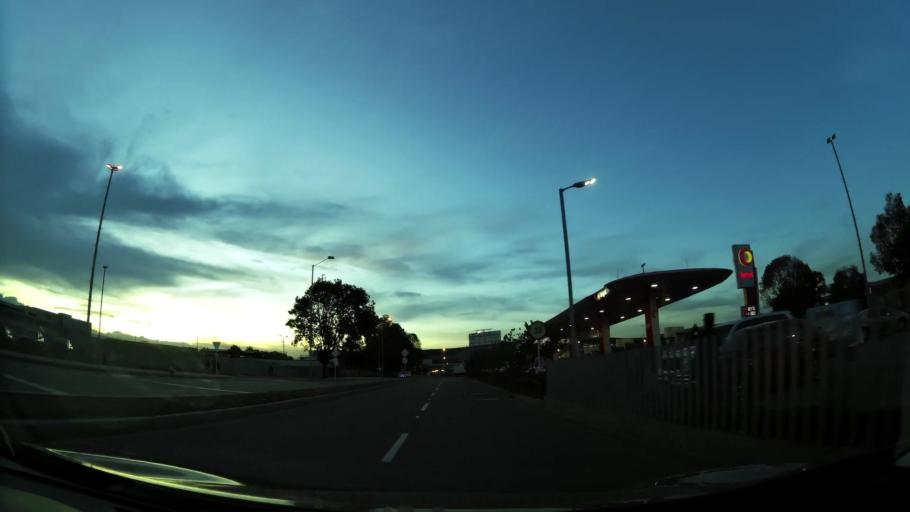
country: CO
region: Cundinamarca
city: Funza
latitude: 4.6950
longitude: -74.1402
